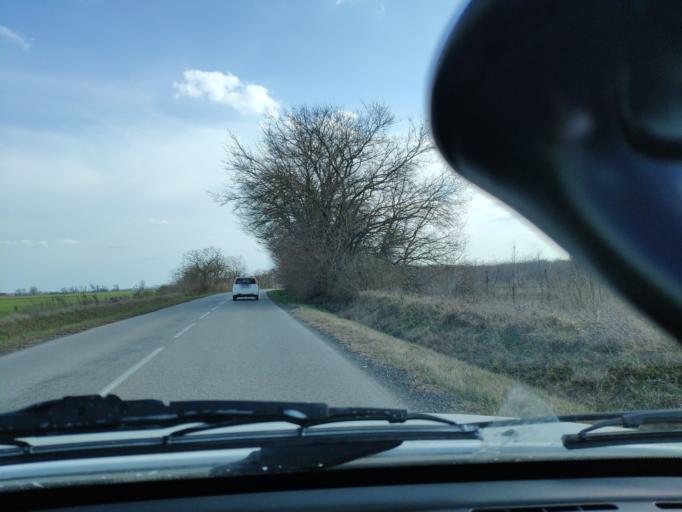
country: HU
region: Pest
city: Rackeve
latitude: 47.1449
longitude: 18.9116
